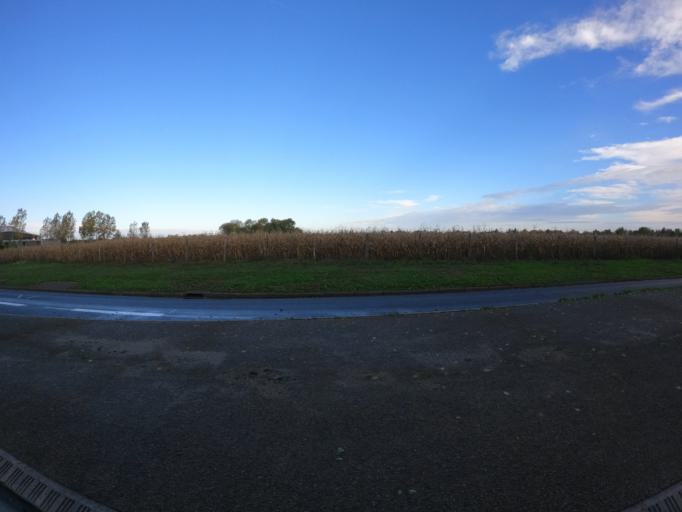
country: FR
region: Ile-de-France
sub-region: Departement de Seine-et-Marne
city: Serris
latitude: 48.8455
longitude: 2.8029
